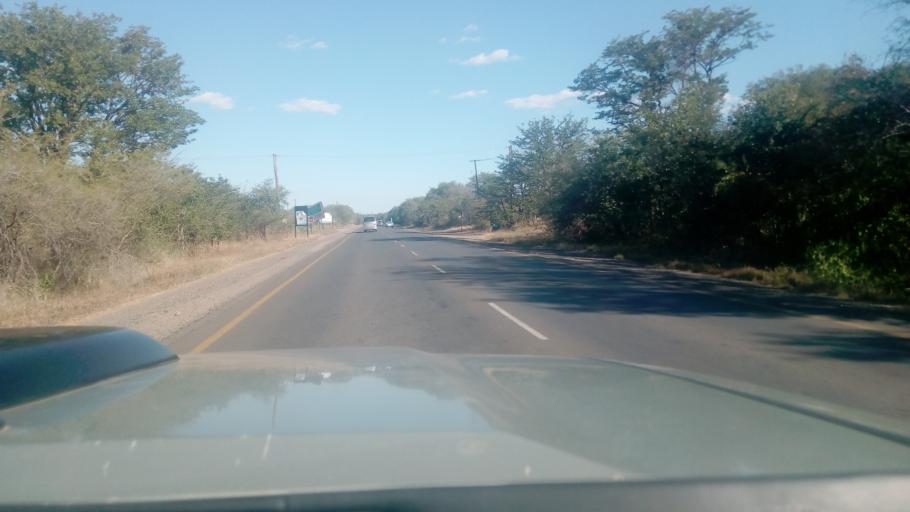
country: ZW
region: Matabeleland North
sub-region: Hwange District
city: Victoria Falls
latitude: -17.9182
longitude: 25.8667
